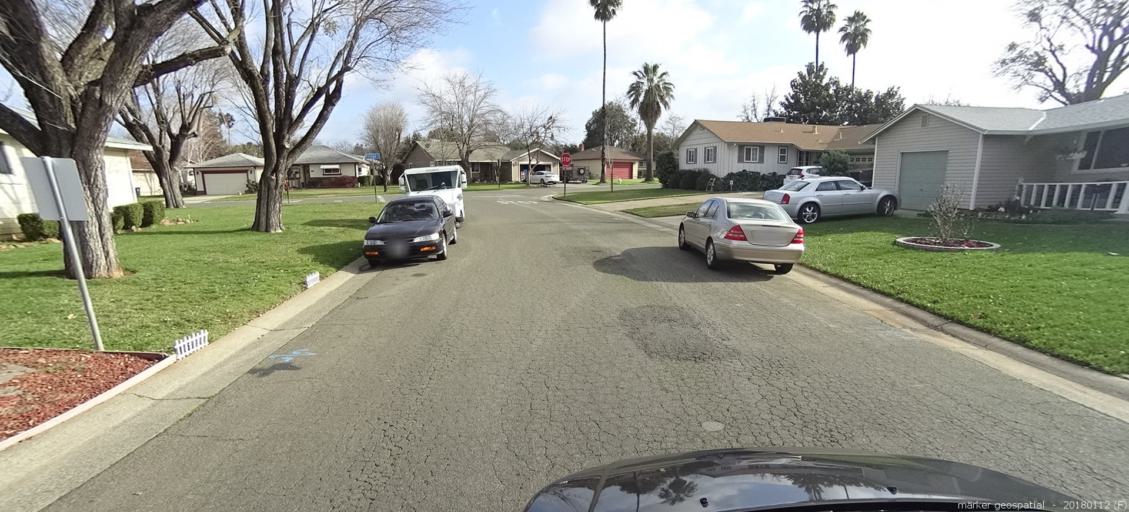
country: US
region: California
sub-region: Sacramento County
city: Rancho Cordova
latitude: 38.5954
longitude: -121.3002
